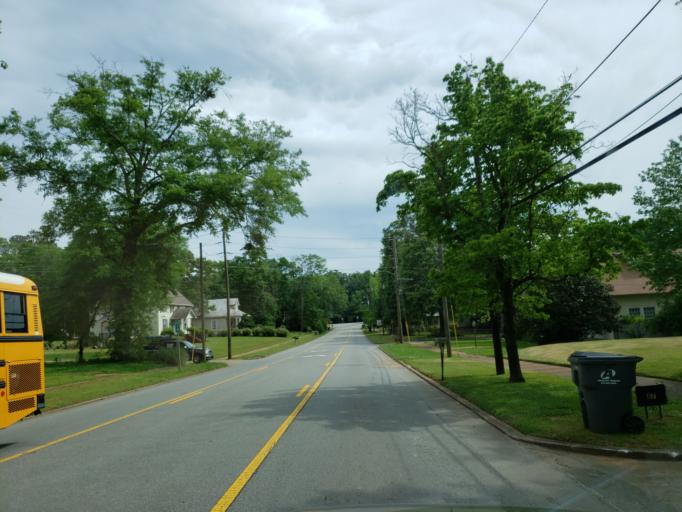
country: US
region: Georgia
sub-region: Monroe County
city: Forsyth
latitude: 33.0318
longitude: -83.9385
